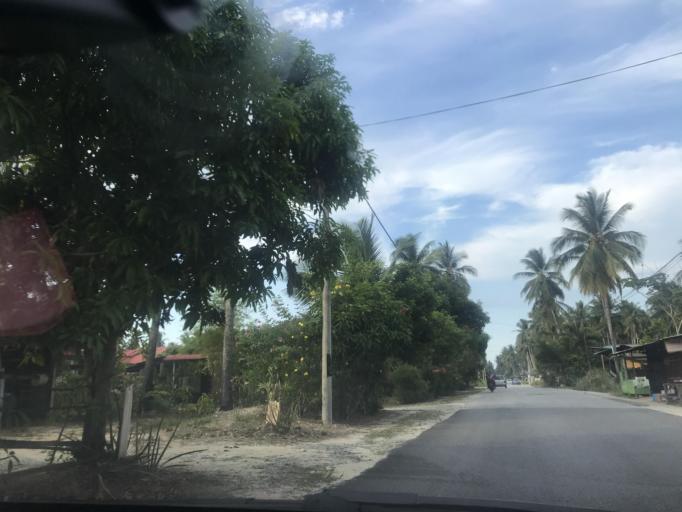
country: MY
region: Kelantan
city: Kota Bharu
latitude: 6.1272
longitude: 102.3579
